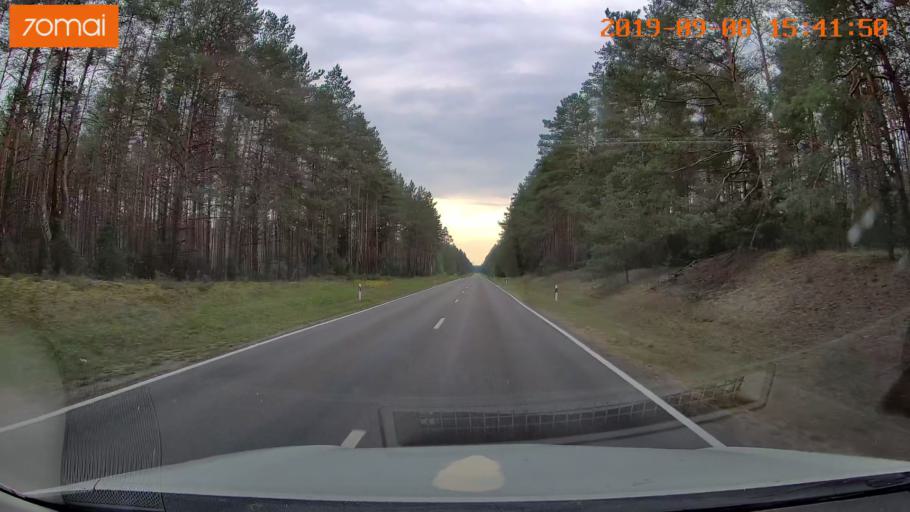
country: LT
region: Alytaus apskritis
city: Druskininkai
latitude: 53.9766
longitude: 24.0000
